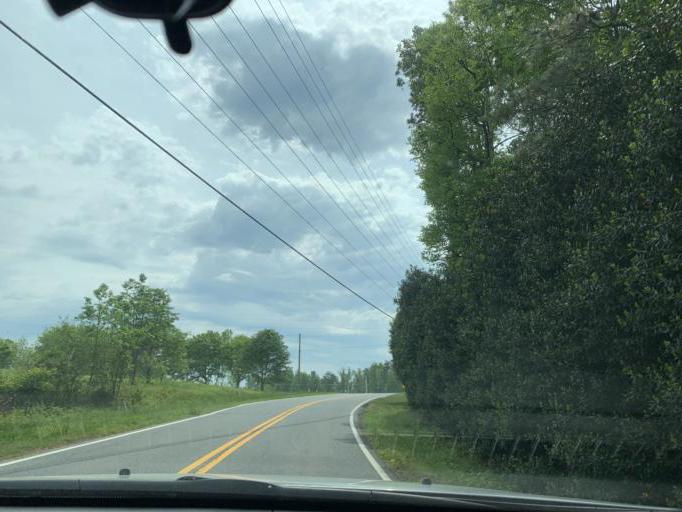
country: US
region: Georgia
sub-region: Forsyth County
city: Cumming
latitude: 34.1360
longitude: -84.1762
